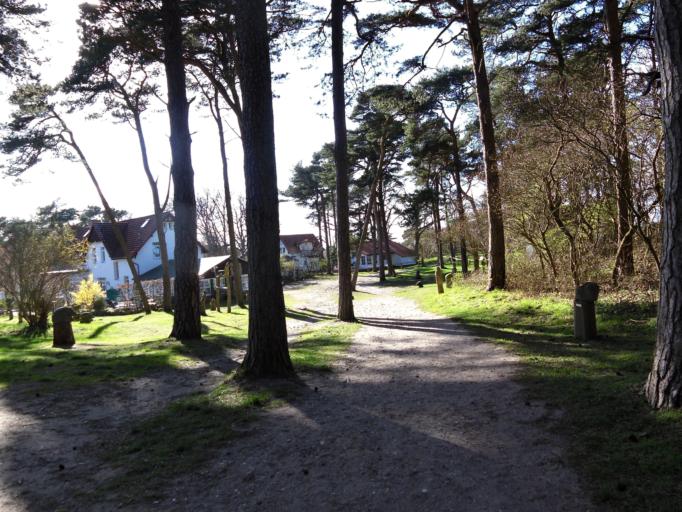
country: DE
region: Mecklenburg-Vorpommern
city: Hiddensee
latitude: 54.5973
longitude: 13.1159
